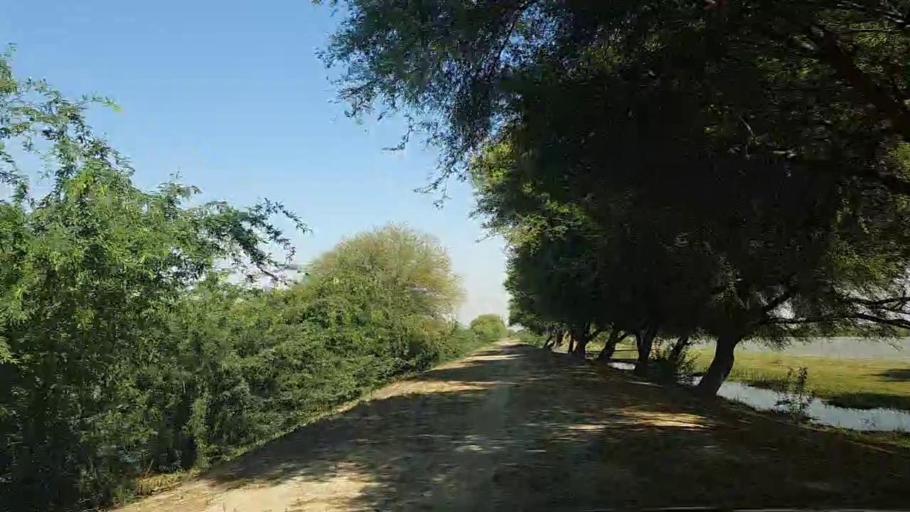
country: PK
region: Sindh
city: Thatta
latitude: 24.7995
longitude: 67.9806
